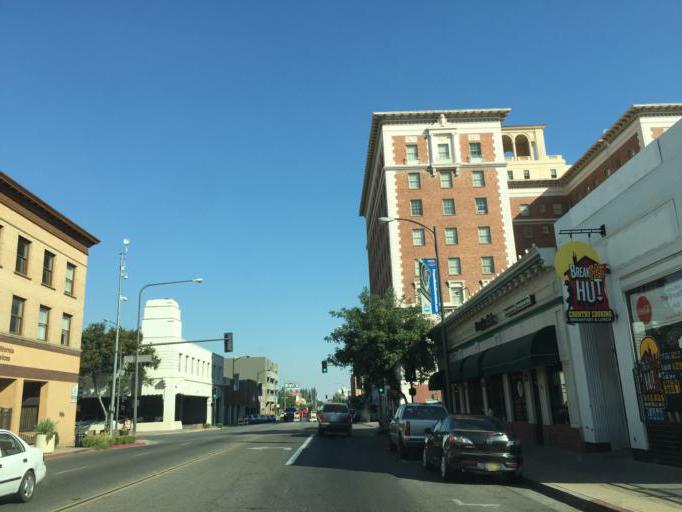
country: US
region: California
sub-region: Fresno County
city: Fresno
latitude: 36.7340
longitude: -119.7884
